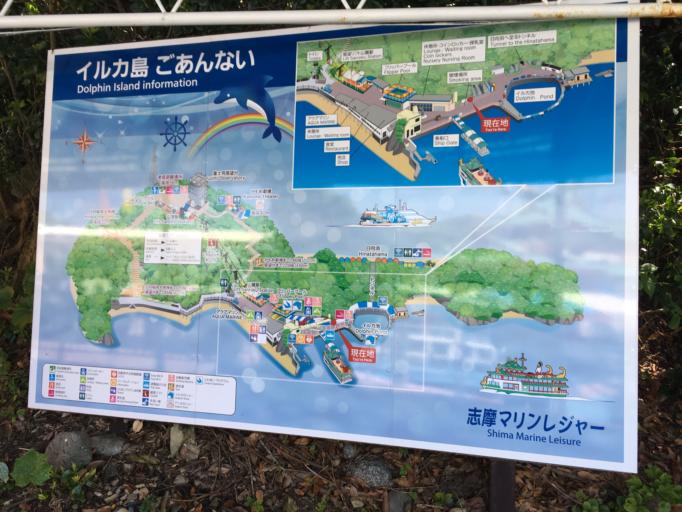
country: JP
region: Mie
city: Toba
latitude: 34.5044
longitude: 136.8355
